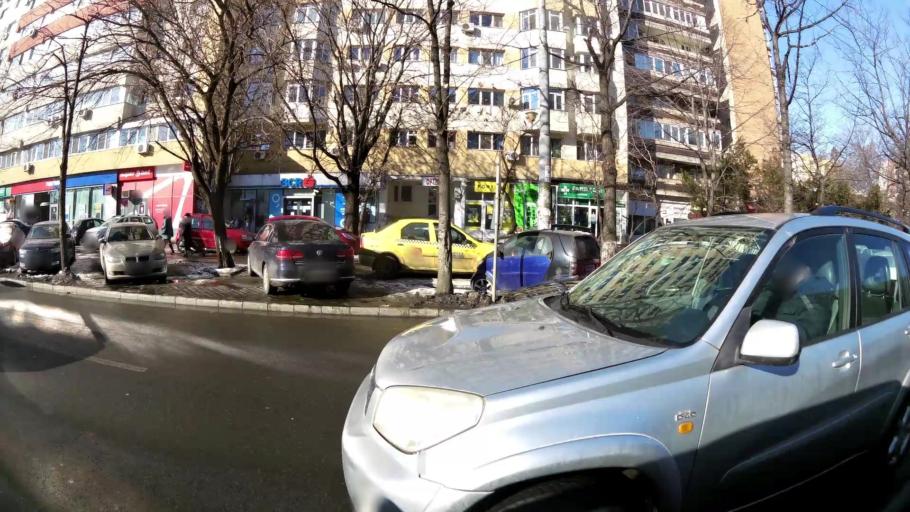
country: RO
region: Bucuresti
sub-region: Municipiul Bucuresti
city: Bucharest
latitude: 44.4556
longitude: 26.1289
